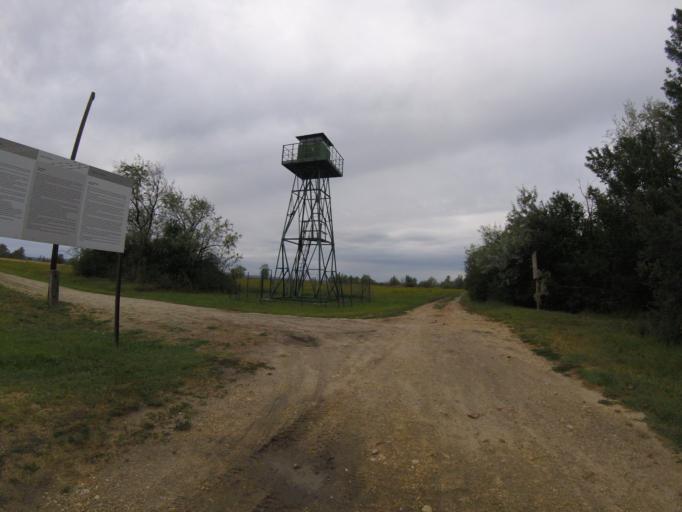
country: HU
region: Gyor-Moson-Sopron
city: Fertod
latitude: 47.6428
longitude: 16.7875
